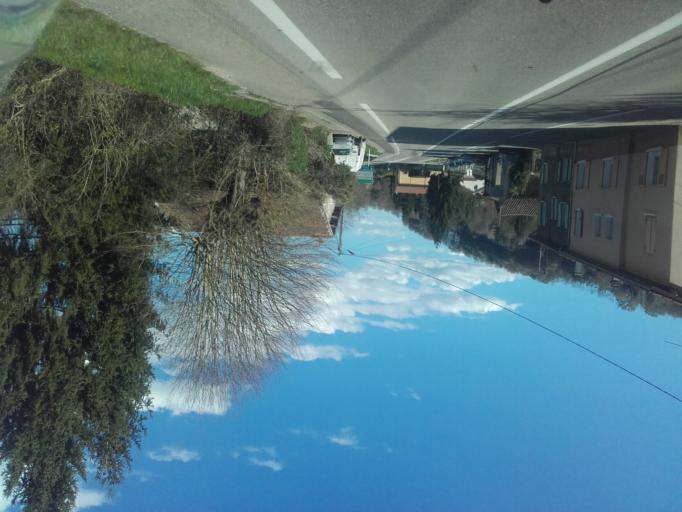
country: FR
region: Rhone-Alpes
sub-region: Departement de l'Isere
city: Nivolas-Vermelle
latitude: 45.5366
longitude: 5.3102
